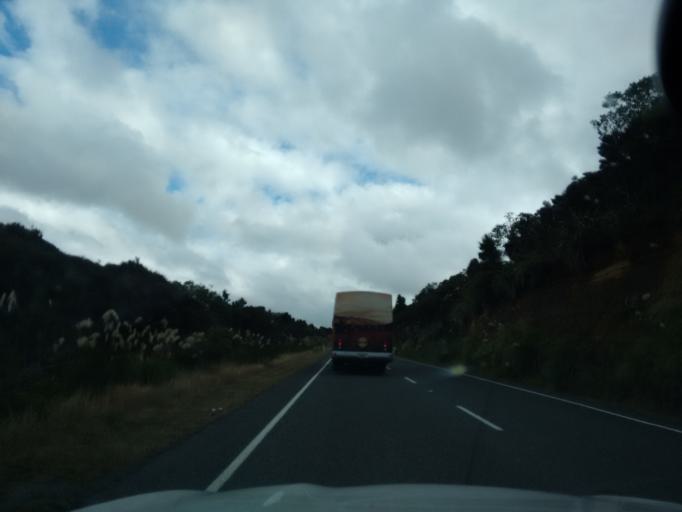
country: NZ
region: Waikato
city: Turangi
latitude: -39.0590
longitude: 175.5796
